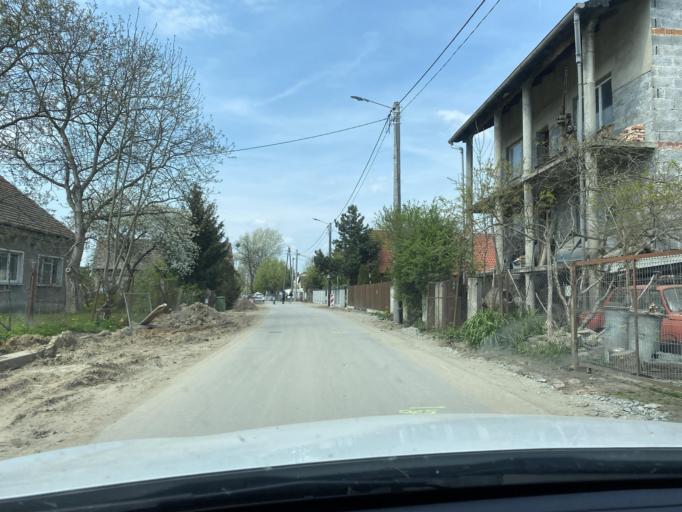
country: PL
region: Lower Silesian Voivodeship
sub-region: Powiat wroclawski
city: Mirkow
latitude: 51.1588
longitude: 17.1719
